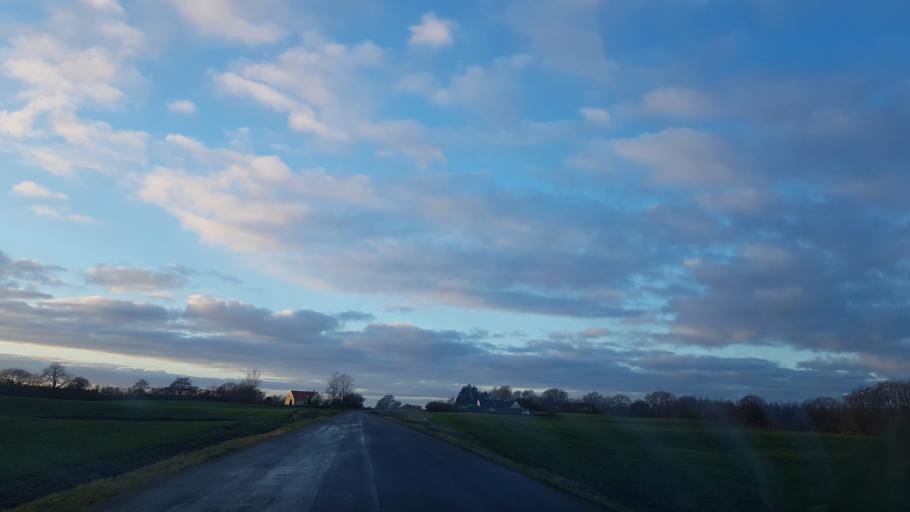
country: DK
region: South Denmark
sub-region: Kolding Kommune
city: Vamdrup
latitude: 55.3683
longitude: 9.3136
